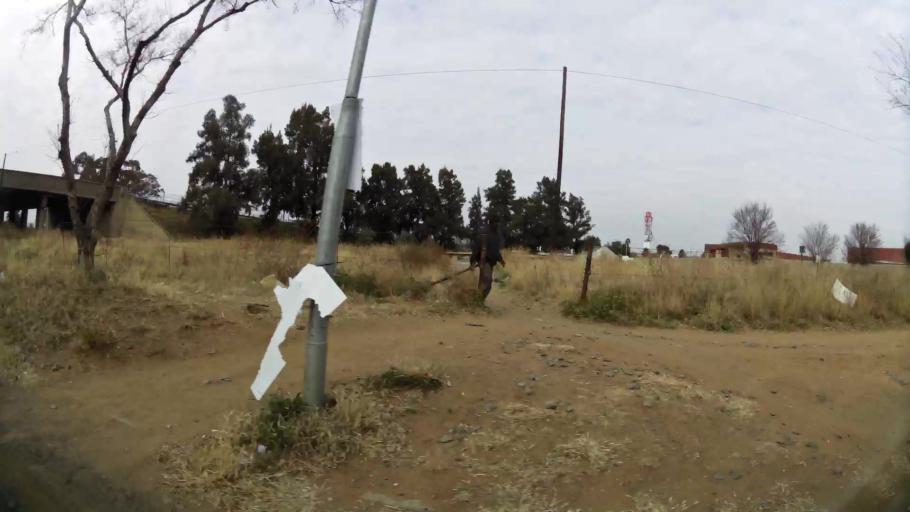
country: ZA
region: Orange Free State
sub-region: Mangaung Metropolitan Municipality
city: Bloemfontein
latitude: -29.1329
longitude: 26.2063
